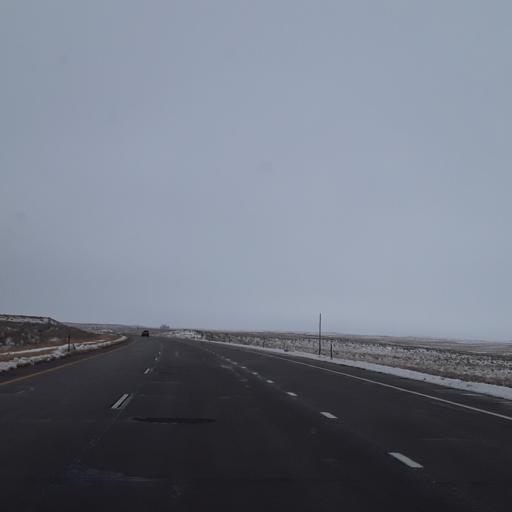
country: US
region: Colorado
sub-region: Logan County
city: Sterling
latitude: 40.6261
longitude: -103.1678
